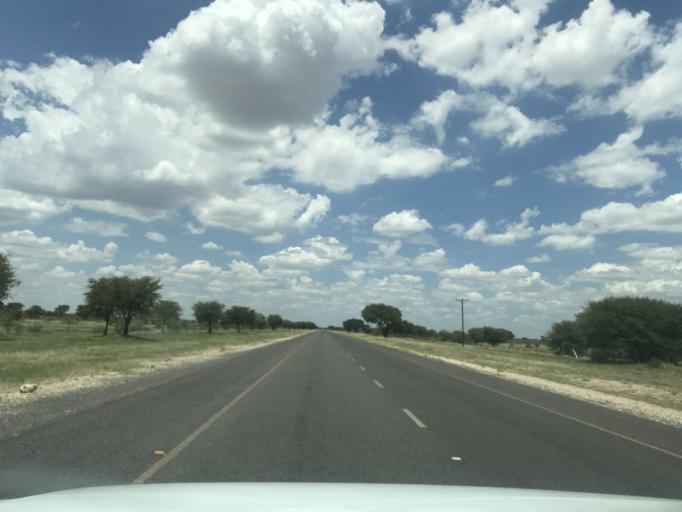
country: BW
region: South East
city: Janeng
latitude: -25.6935
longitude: 25.1281
